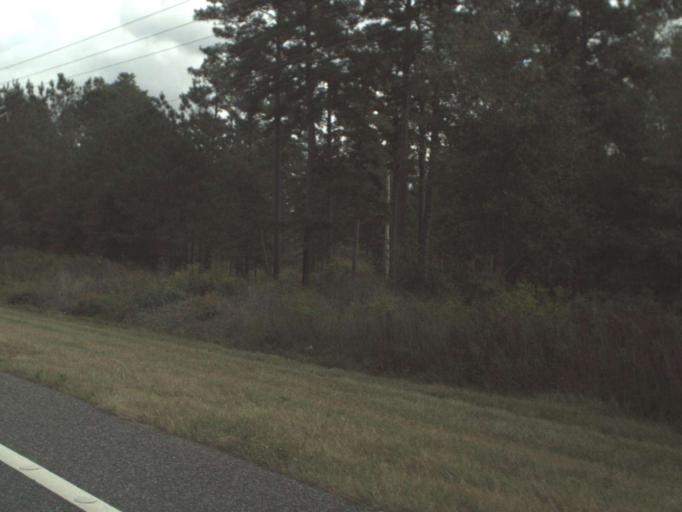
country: US
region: Florida
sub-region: Leon County
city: Tallahassee
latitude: 30.5786
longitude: -84.2005
